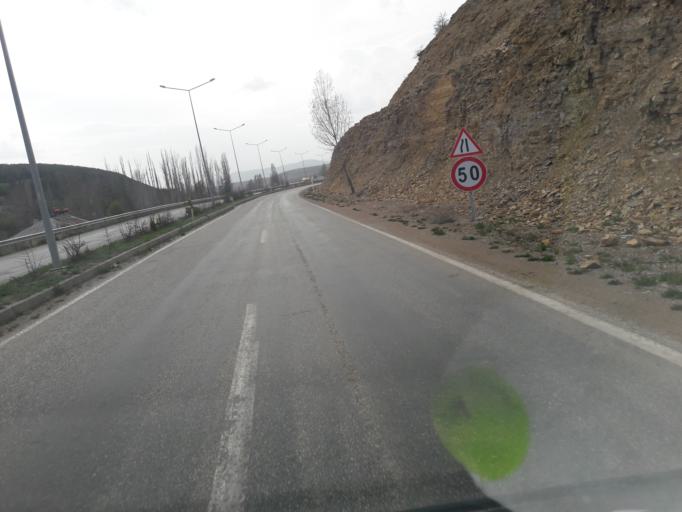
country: TR
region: Gumushane
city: Siran
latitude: 40.1767
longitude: 39.1309
